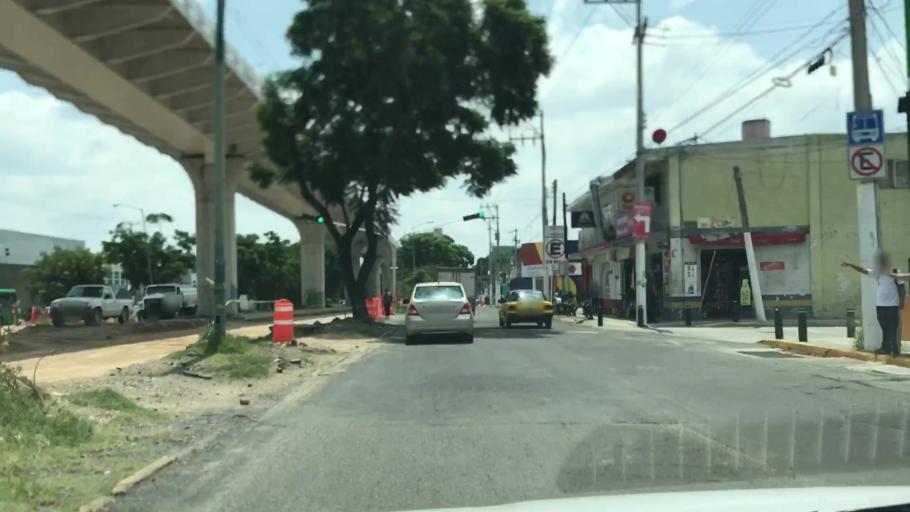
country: MX
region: Jalisco
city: Zapopan2
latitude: 20.7364
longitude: -103.4009
